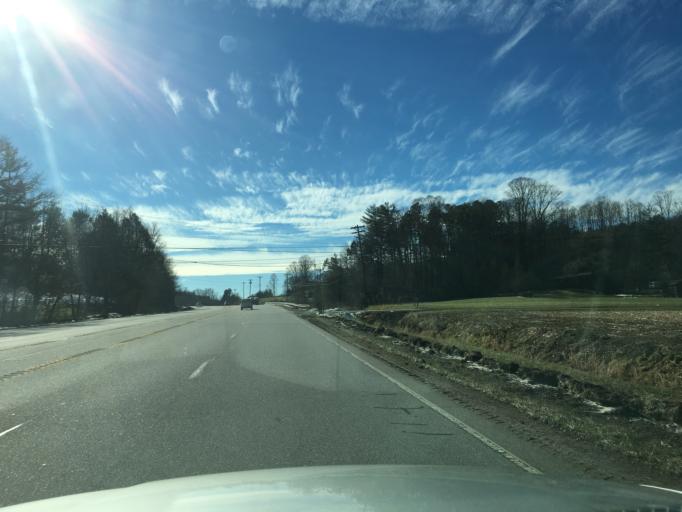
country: US
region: North Carolina
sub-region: Henderson County
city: Etowah
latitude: 35.3361
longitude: -82.6349
